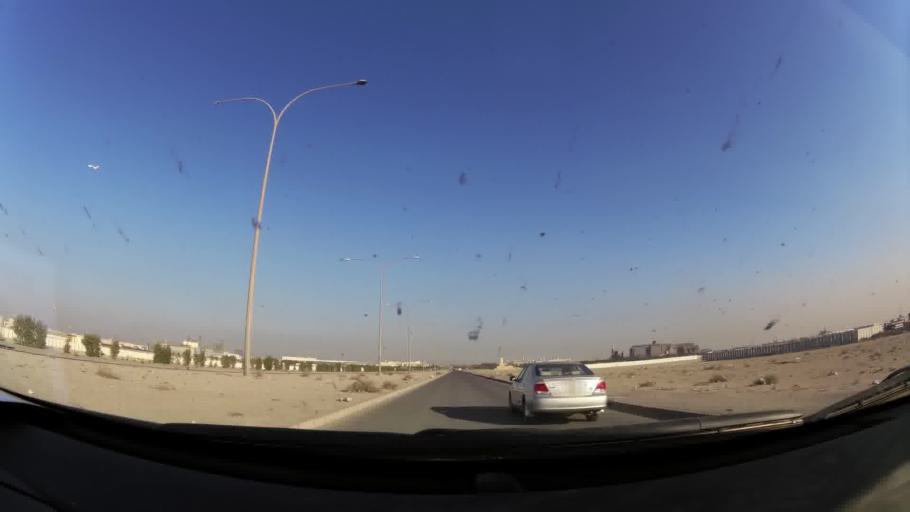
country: KW
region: Al Ahmadi
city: Al Ahmadi
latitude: 28.9956
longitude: 48.1156
